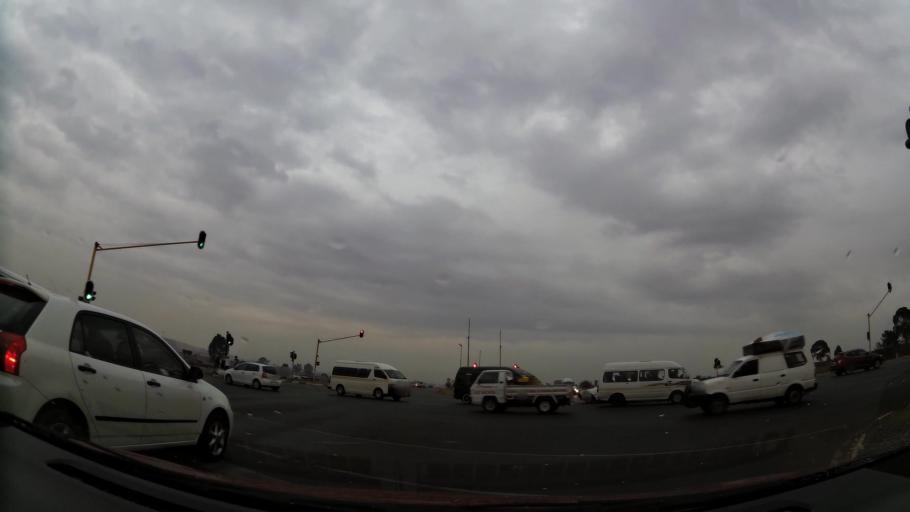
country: ZA
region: Gauteng
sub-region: City of Johannesburg Metropolitan Municipality
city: Roodepoort
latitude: -26.1750
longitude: 27.8089
